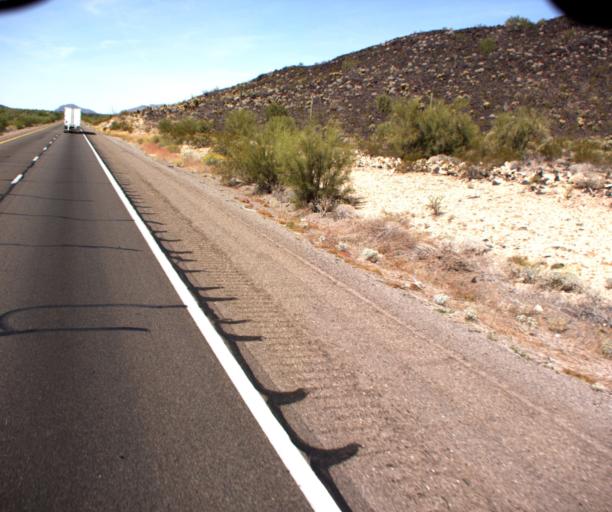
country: US
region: Arizona
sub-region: La Paz County
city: Salome
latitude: 33.6487
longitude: -113.8999
